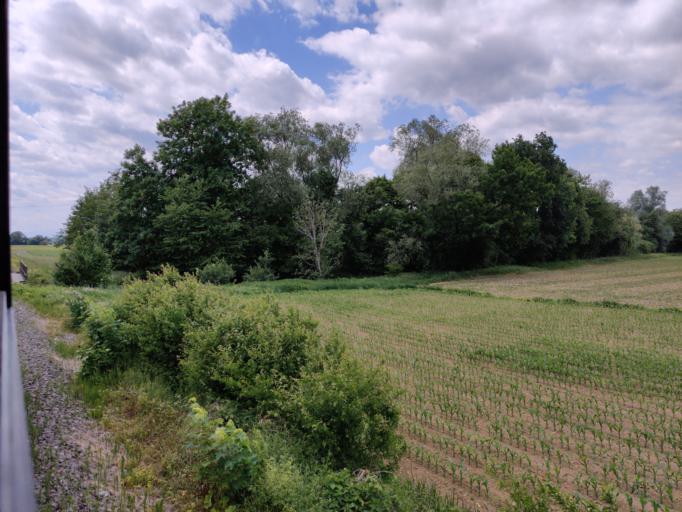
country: AT
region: Styria
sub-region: Politischer Bezirk Suedoststeiermark
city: Deutsch Goritz
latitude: 46.7319
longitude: 15.8509
